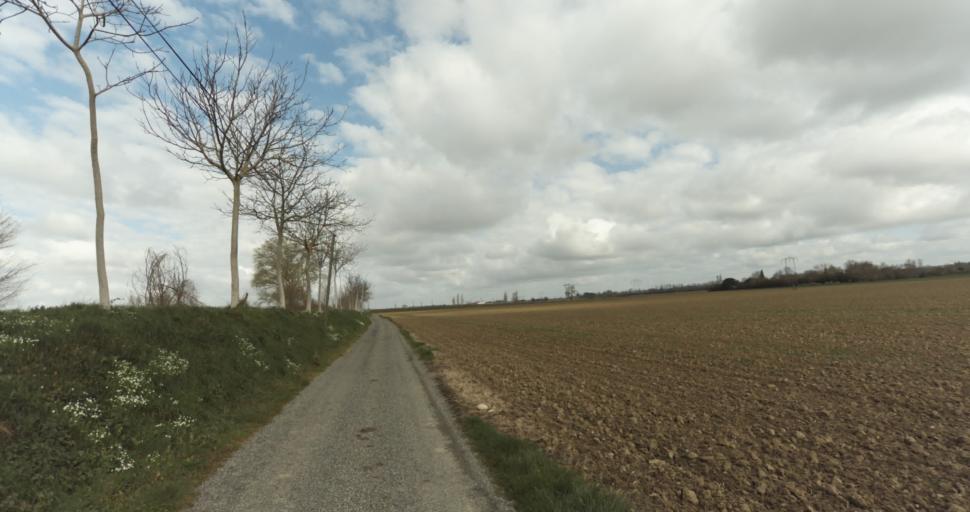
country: FR
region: Midi-Pyrenees
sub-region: Departement de la Haute-Garonne
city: Auterive
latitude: 43.3429
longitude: 1.4481
